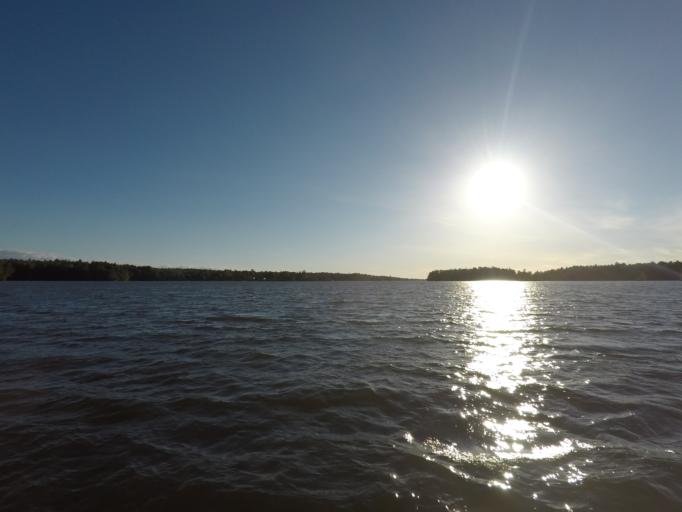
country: SE
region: Soedermanland
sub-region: Eskilstuna Kommun
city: Kvicksund
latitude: 59.4570
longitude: 16.3790
